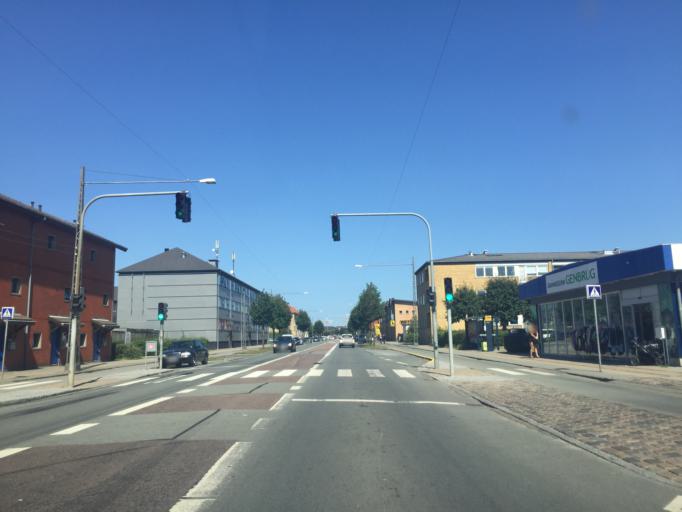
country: DK
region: Capital Region
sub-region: Tarnby Kommune
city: Tarnby
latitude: 55.6377
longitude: 12.5887
